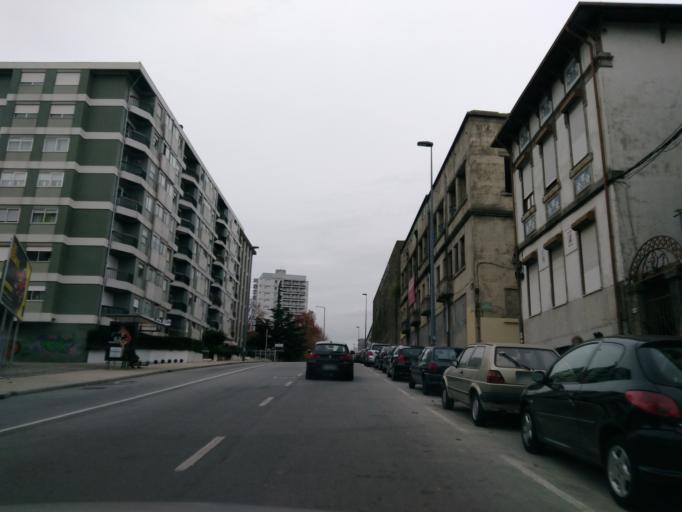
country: PT
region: Porto
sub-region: Porto
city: Porto
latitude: 41.1513
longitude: -8.5975
